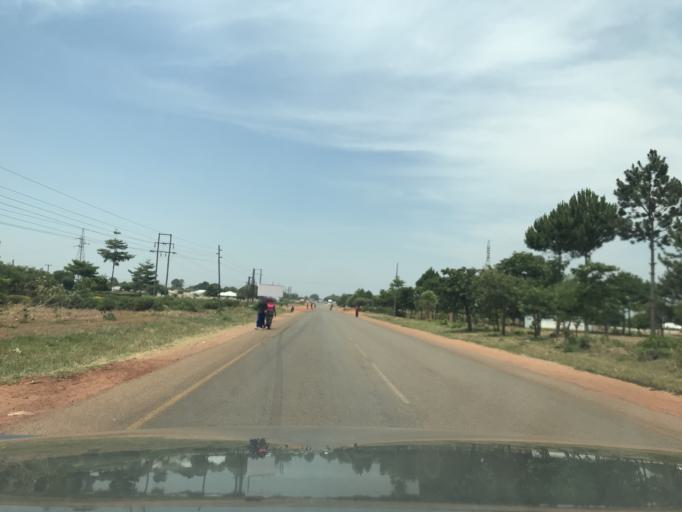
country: ZM
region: Northern
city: Kasama
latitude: -10.2131
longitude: 31.1569
